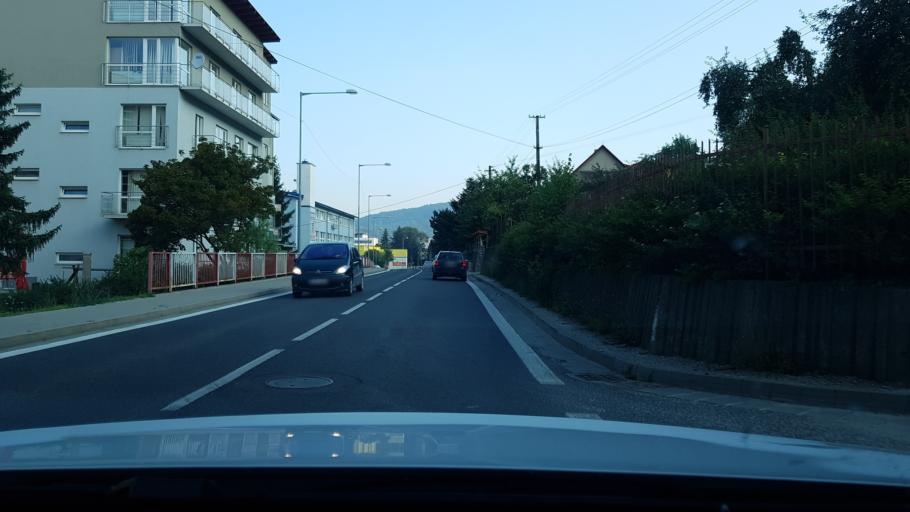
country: SK
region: Trenciansky
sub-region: Okres Povazska Bystrica
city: Povazska Bystrica
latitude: 49.1135
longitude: 18.4527
